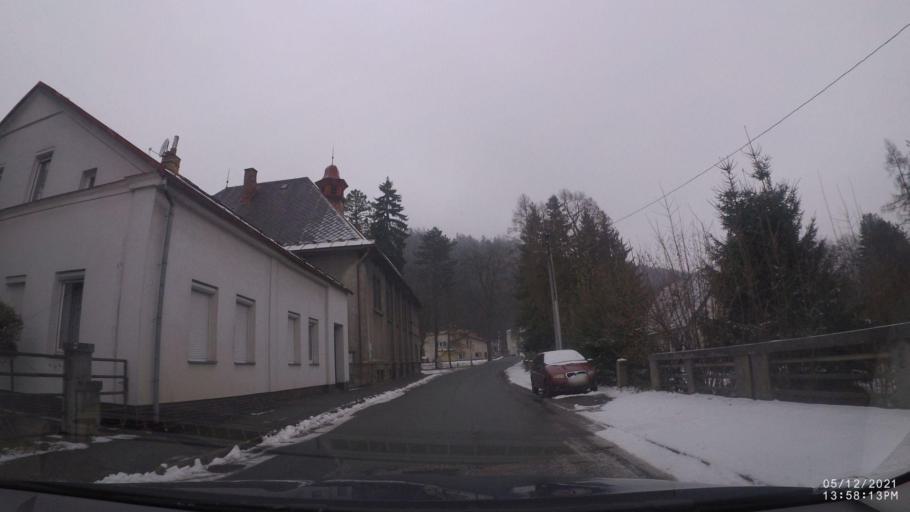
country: CZ
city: Hronov
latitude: 50.4833
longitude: 16.1809
